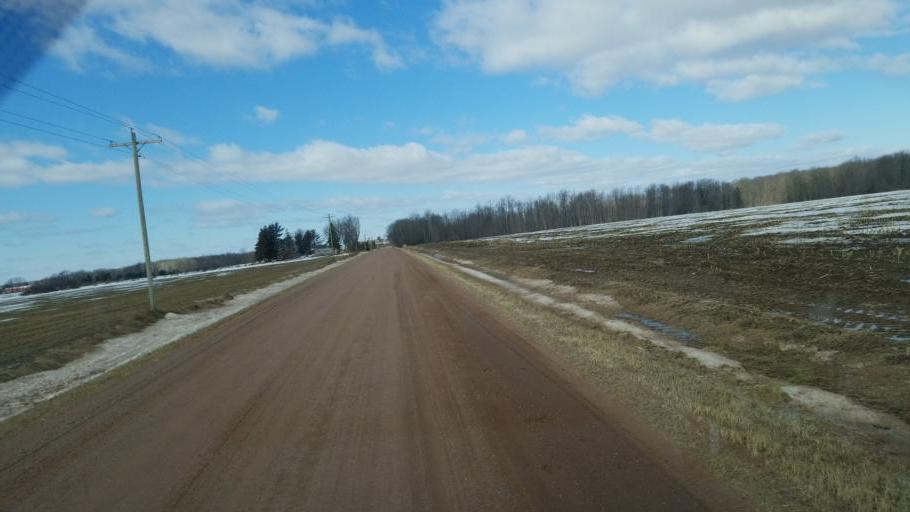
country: US
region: Wisconsin
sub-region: Clark County
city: Loyal
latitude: 44.6835
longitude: -90.4372
